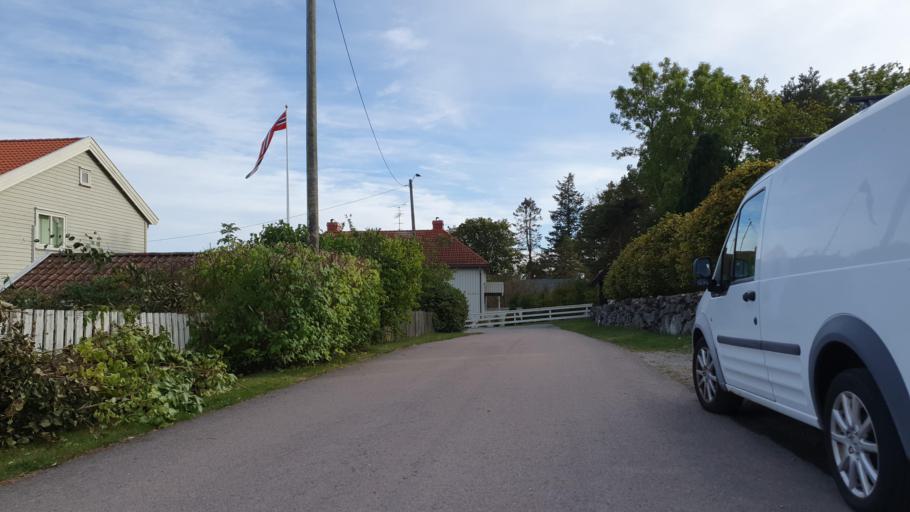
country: NO
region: Vestfold
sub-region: Tonsberg
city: Tonsberg
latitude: 59.2795
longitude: 10.4175
